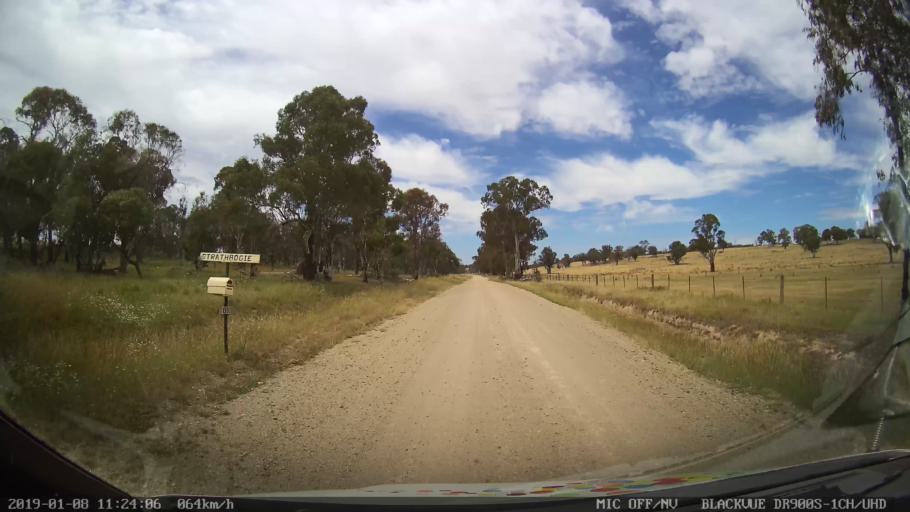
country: AU
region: New South Wales
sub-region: Guyra
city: Guyra
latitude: -30.2615
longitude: 151.5583
